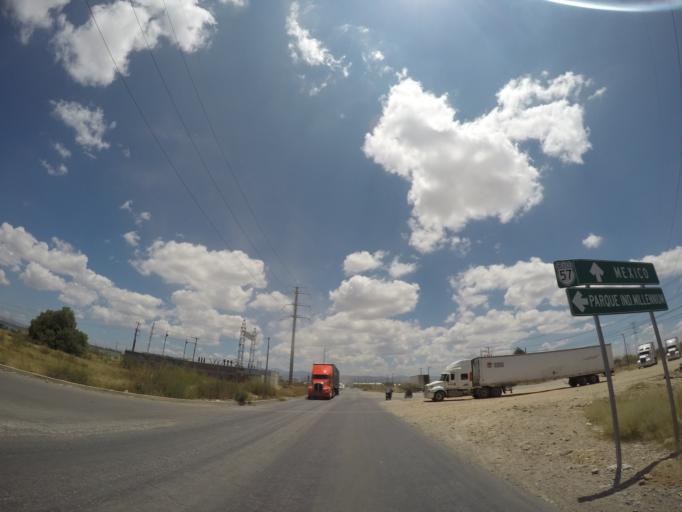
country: MX
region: San Luis Potosi
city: La Pila
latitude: 22.0414
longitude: -100.8898
